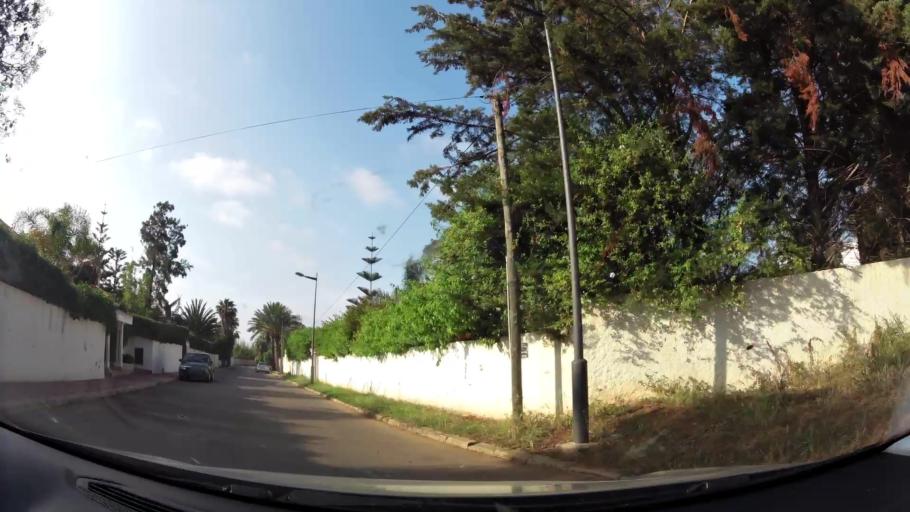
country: MA
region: Rabat-Sale-Zemmour-Zaer
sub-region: Rabat
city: Rabat
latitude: 33.9417
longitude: -6.8142
